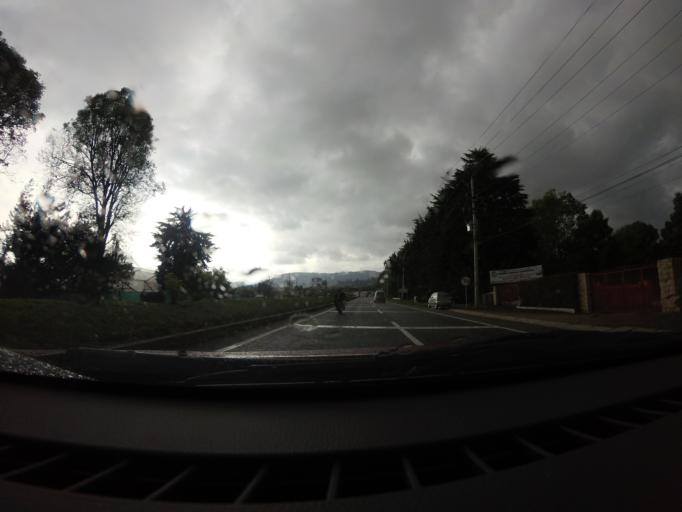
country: CO
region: Cundinamarca
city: El Rosal
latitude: 4.8495
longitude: -74.2720
